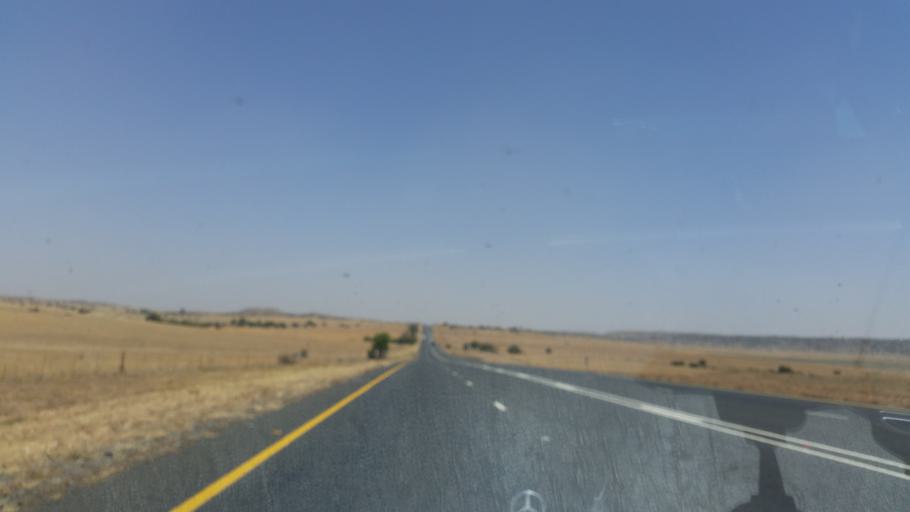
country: ZA
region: Orange Free State
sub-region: Lejweleputswa District Municipality
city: Winburg
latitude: -28.6831
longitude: 26.8262
